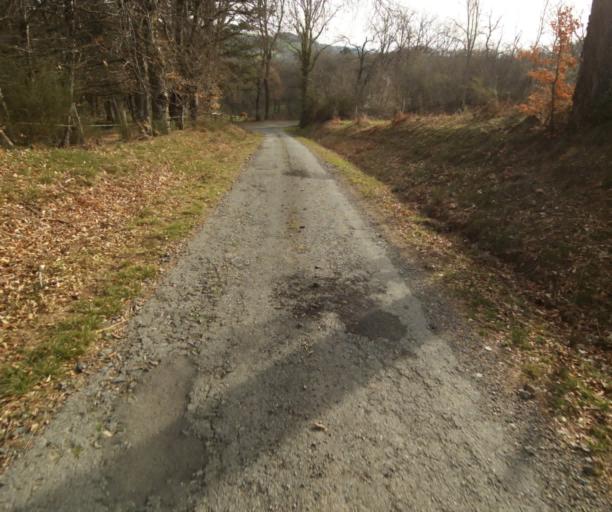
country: FR
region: Limousin
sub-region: Departement de la Correze
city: Chamboulive
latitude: 45.4413
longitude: 1.7480
